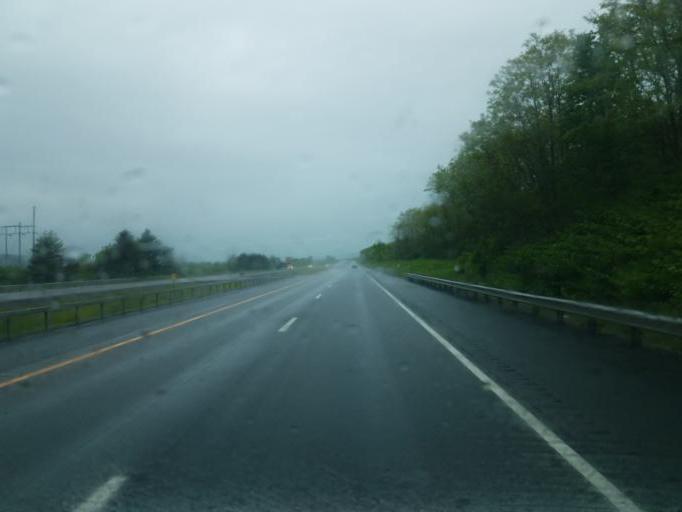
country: US
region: New York
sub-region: Herkimer County
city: Frankfort
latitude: 43.0365
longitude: -75.0490
